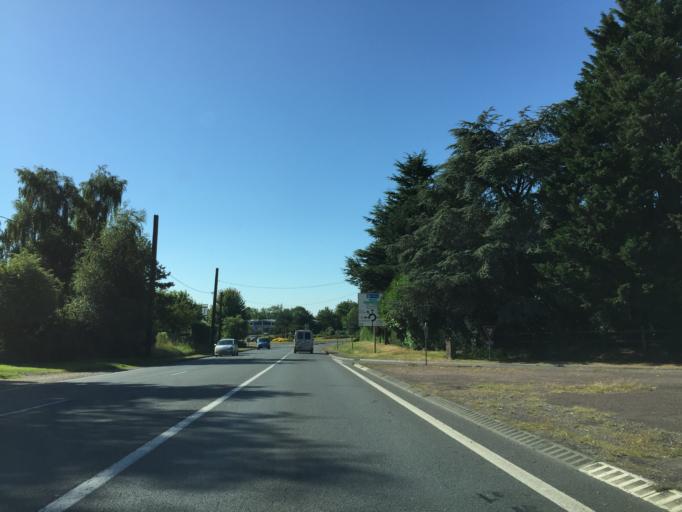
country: FR
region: Lower Normandy
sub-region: Departement du Calvados
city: Beuvillers
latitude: 49.1485
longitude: 0.2551
